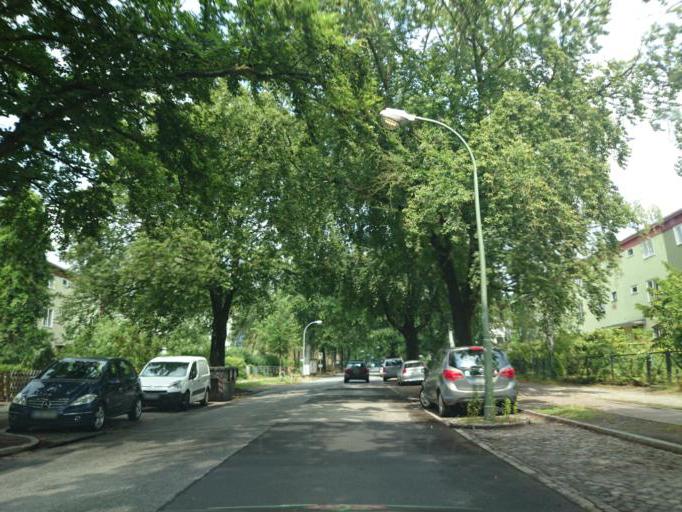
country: DE
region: Berlin
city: Zehlendorf Bezirk
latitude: 52.4476
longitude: 13.2571
